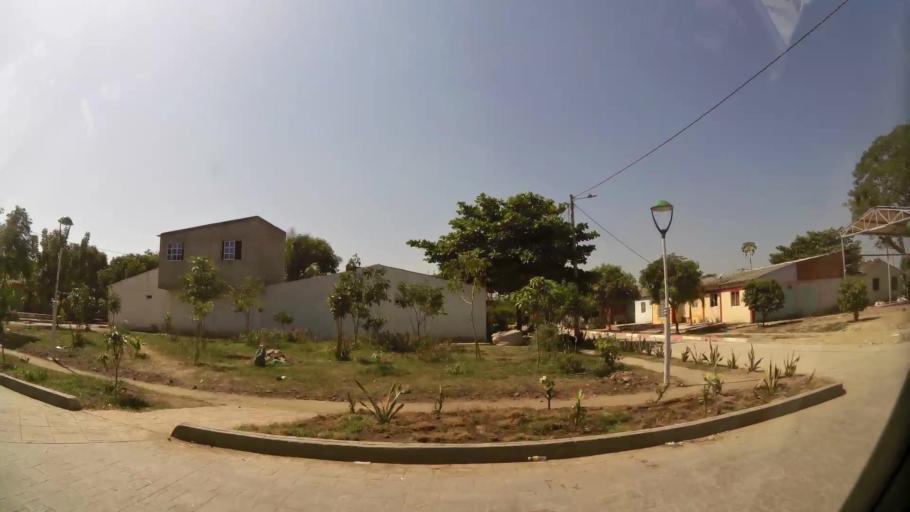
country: CO
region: Bolivar
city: Cartagena
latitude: 10.3919
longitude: -75.4528
